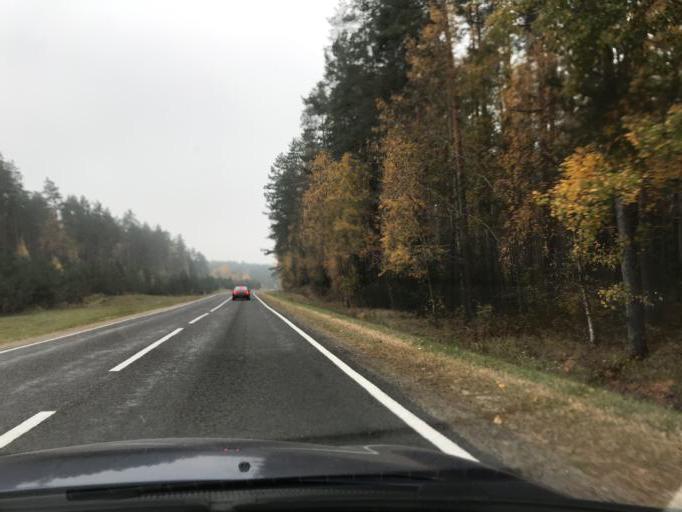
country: LT
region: Alytaus apskritis
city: Druskininkai
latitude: 53.8897
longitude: 23.9102
